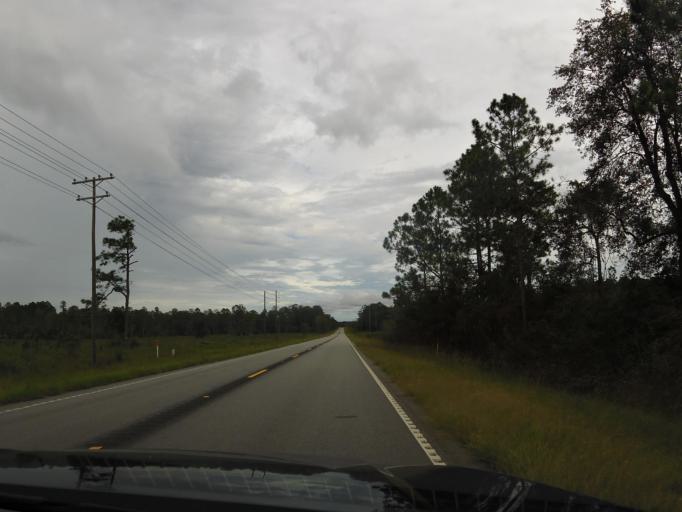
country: US
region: Florida
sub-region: Nassau County
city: Hilliard
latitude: 30.5223
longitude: -82.0767
